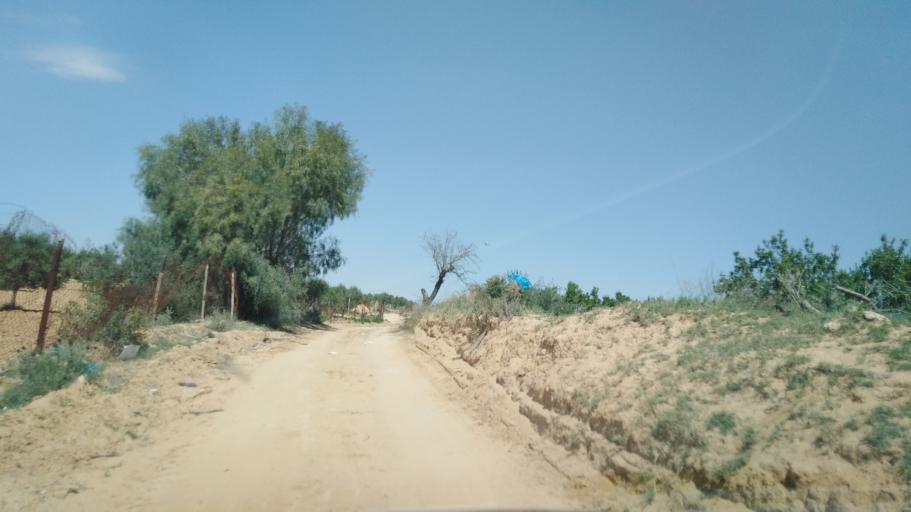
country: TN
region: Safaqis
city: Sfax
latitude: 34.7639
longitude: 10.5198
